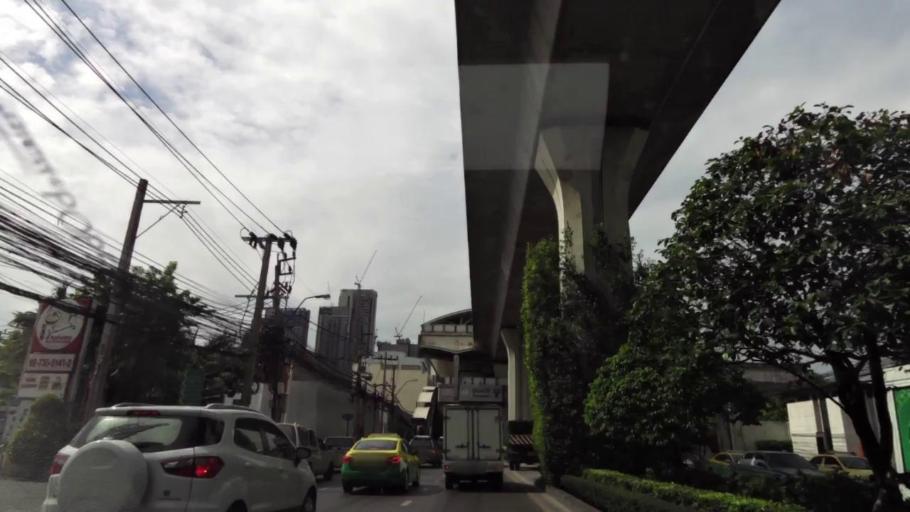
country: TH
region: Bangkok
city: Phra Khanong
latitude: 13.6904
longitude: 100.6085
